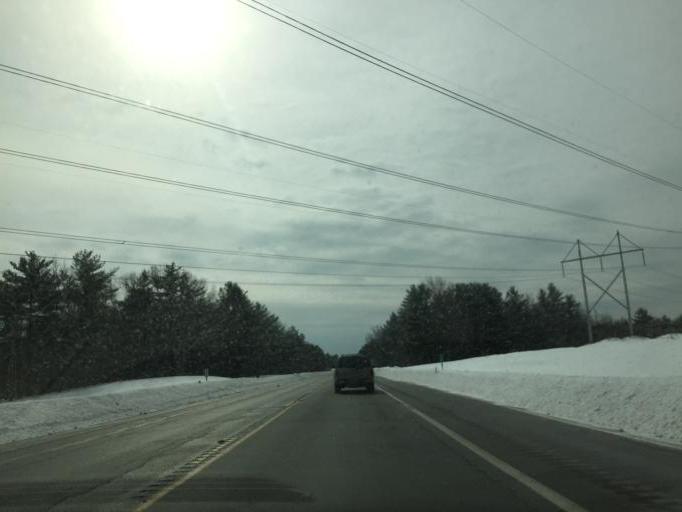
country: US
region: New Hampshire
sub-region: Strafford County
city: Rochester
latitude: 43.3496
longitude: -70.9855
